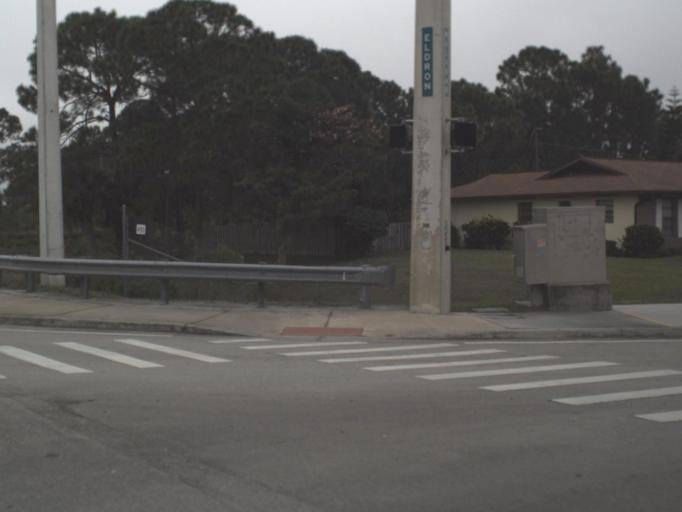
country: US
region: Florida
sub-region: Brevard County
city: West Melbourne
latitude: 27.9990
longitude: -80.6630
